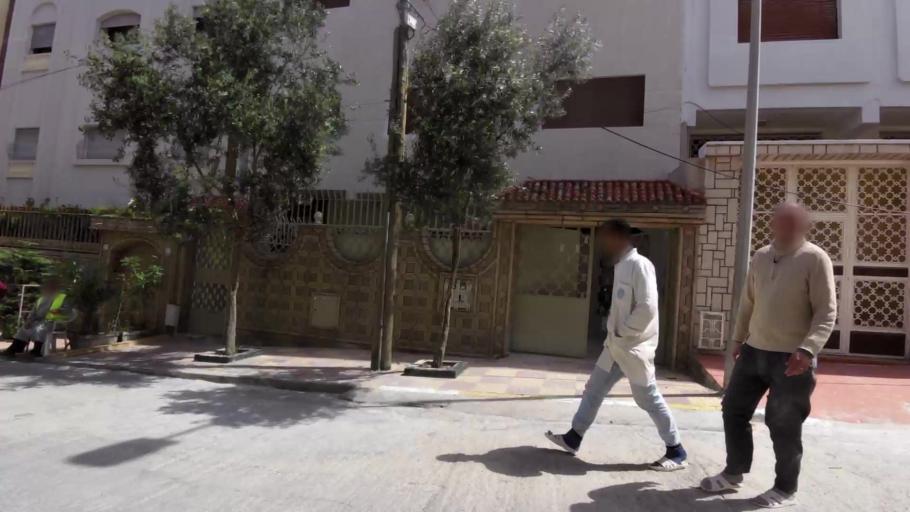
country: MA
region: Tanger-Tetouan
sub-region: Tanger-Assilah
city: Tangier
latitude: 35.7575
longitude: -5.8337
